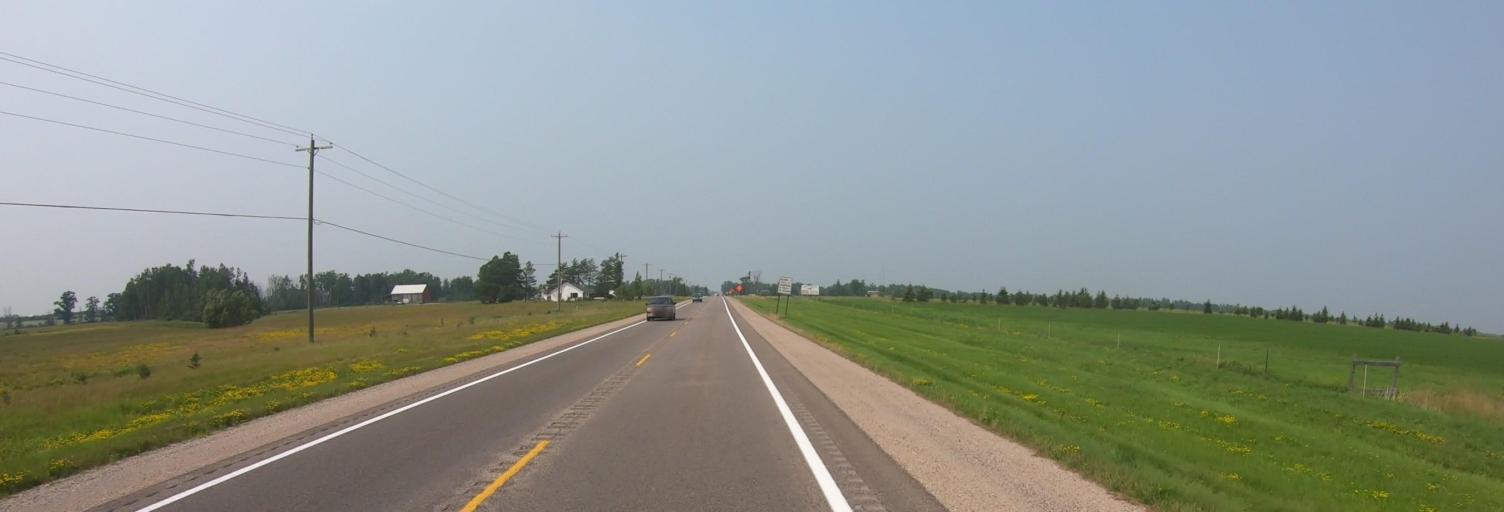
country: US
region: Michigan
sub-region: Chippewa County
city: Sault Ste. Marie
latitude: 46.1347
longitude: -84.3633
